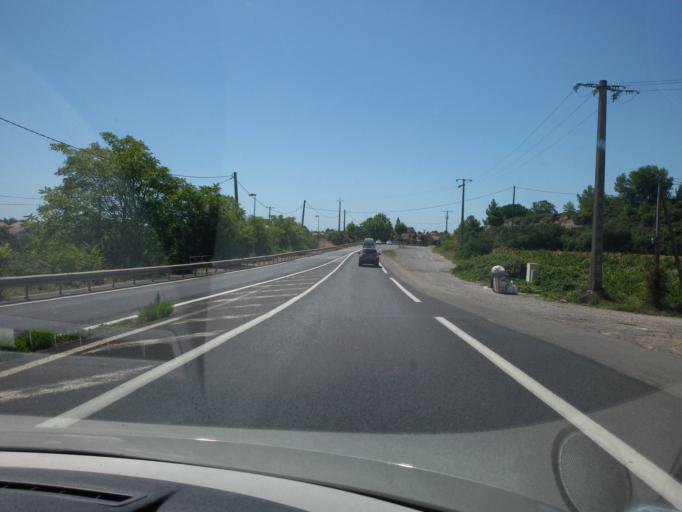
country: FR
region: Languedoc-Roussillon
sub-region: Departement de l'Herault
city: Mireval
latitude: 43.5159
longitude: 3.8070
